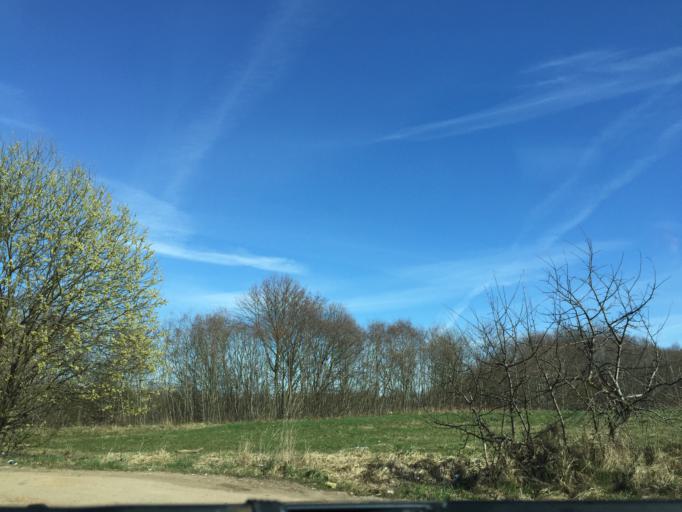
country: LT
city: Varniai
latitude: 55.7866
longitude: 22.6396
